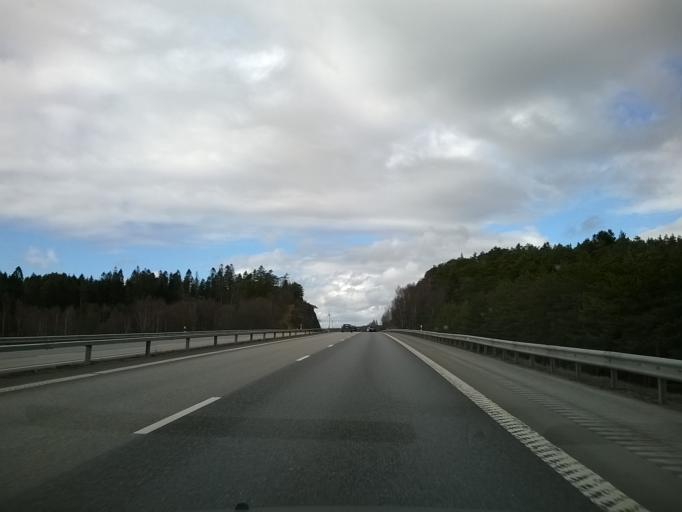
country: SE
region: Halland
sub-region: Kungsbacka Kommun
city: Frillesas
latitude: 57.3092
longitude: 12.2133
